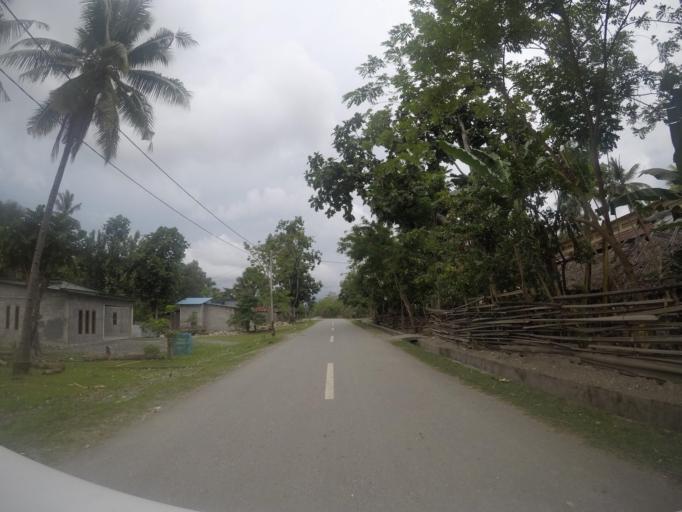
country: TL
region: Viqueque
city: Viqueque
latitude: -8.8606
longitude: 126.3676
